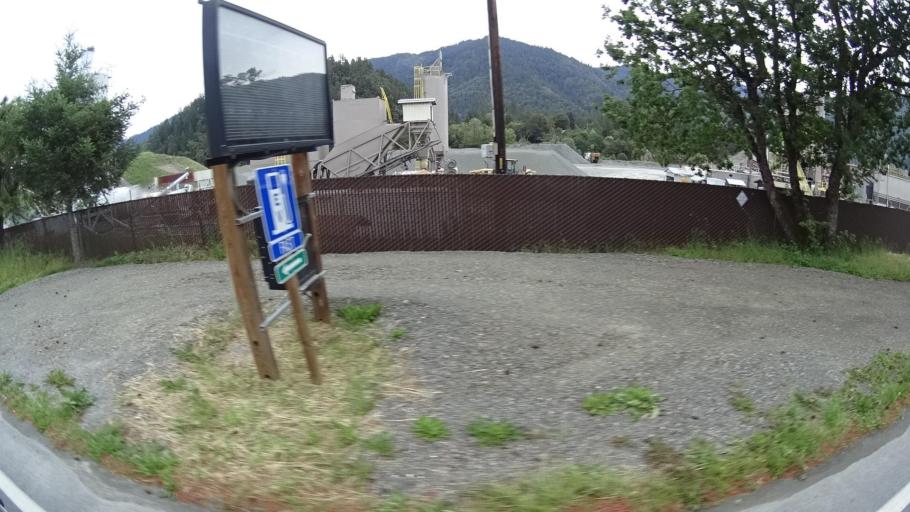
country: US
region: California
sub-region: Humboldt County
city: Willow Creek
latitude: 40.9475
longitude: -123.6363
